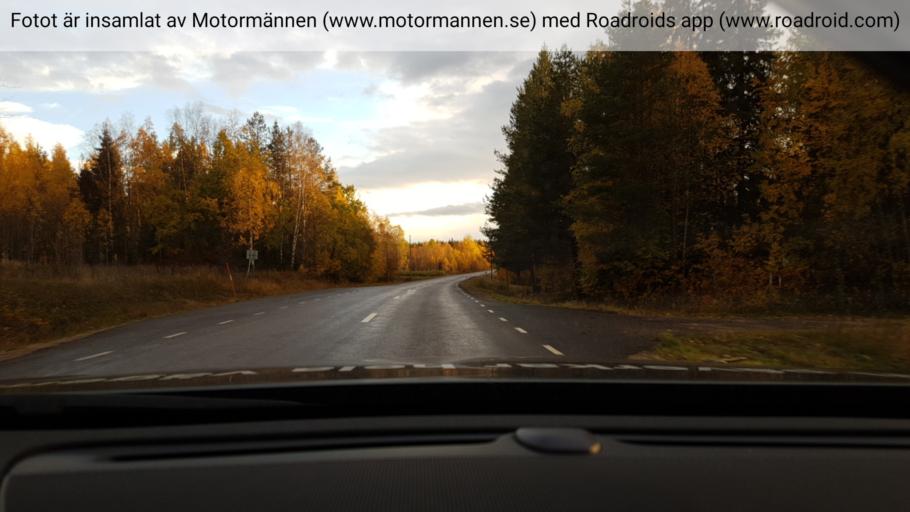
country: SE
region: Norrbotten
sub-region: Overkalix Kommun
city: OEverkalix
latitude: 66.6008
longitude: 22.7626
